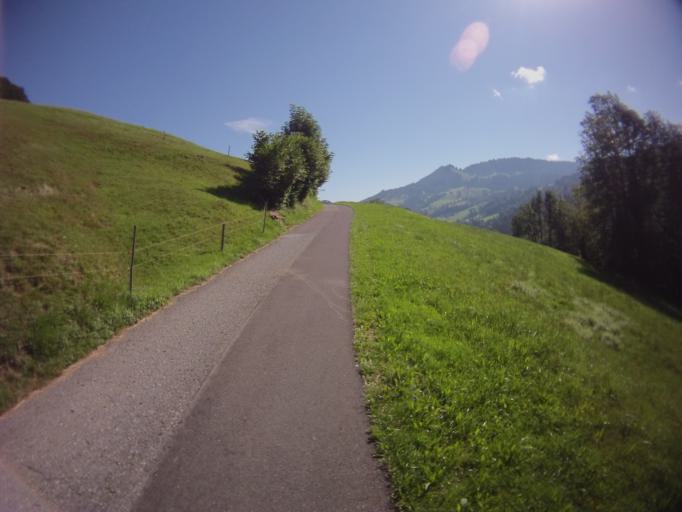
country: CH
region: Schwyz
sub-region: Bezirk Schwyz
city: Sattel
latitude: 47.0875
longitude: 8.6477
